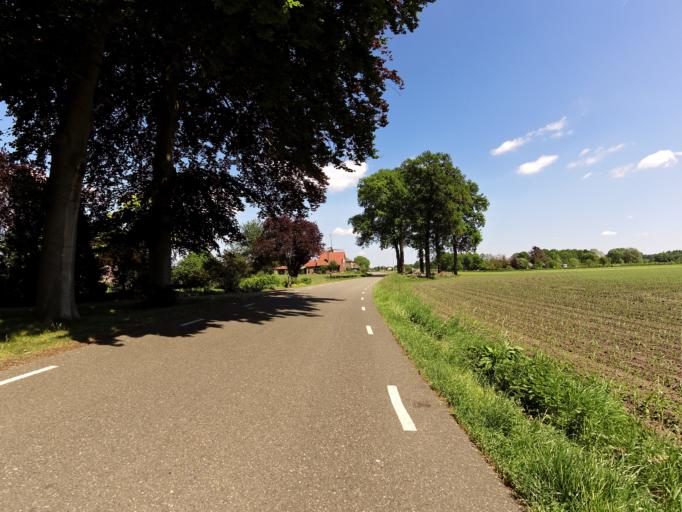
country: NL
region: Gelderland
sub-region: Gemeente Bronckhorst
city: Hengelo
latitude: 52.0812
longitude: 6.3532
